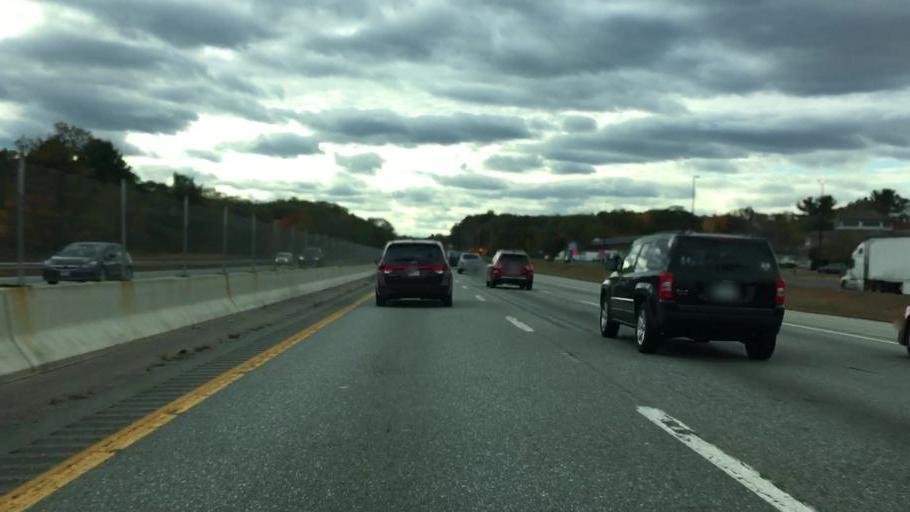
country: US
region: Massachusetts
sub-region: Middlesex County
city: Framingham Center
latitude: 42.3118
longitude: -71.4269
